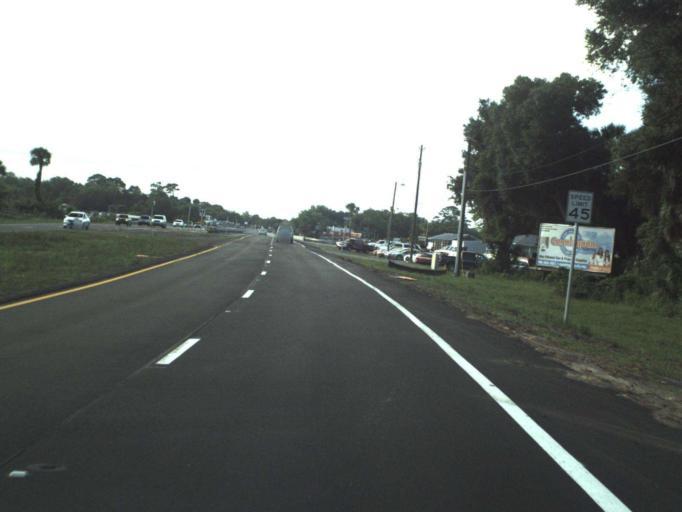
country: US
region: Florida
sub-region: Volusia County
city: Ponce Inlet
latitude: 29.1010
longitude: -80.9707
